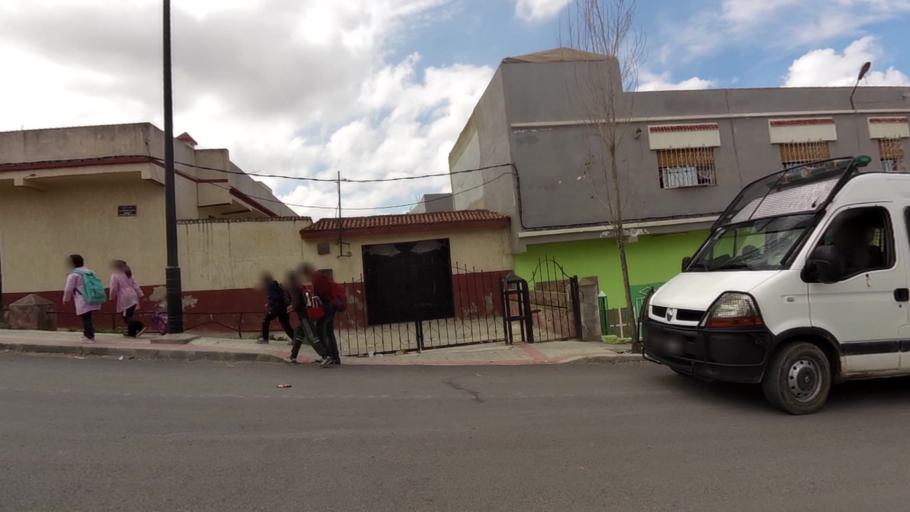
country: MA
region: Tanger-Tetouan
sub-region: Tanger-Assilah
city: Tangier
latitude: 35.7780
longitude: -5.7540
